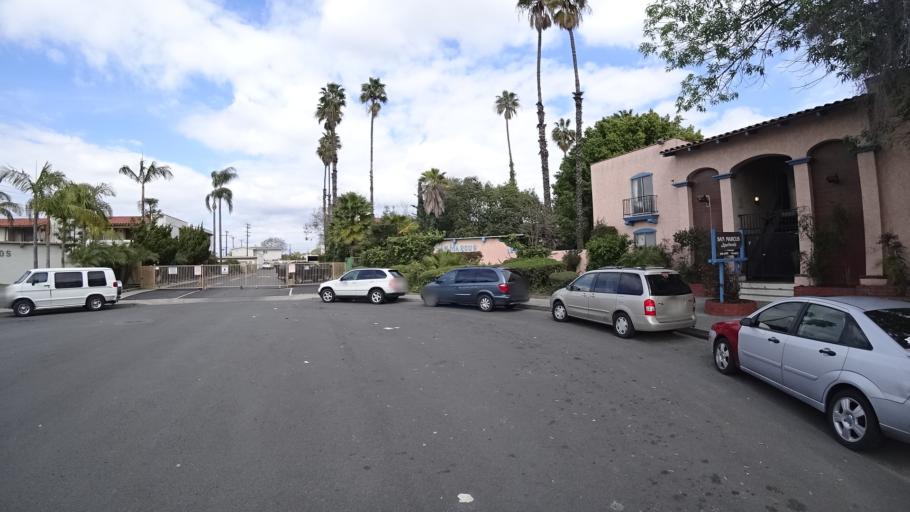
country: US
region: California
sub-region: Orange County
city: Stanton
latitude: 33.8328
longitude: -117.9795
